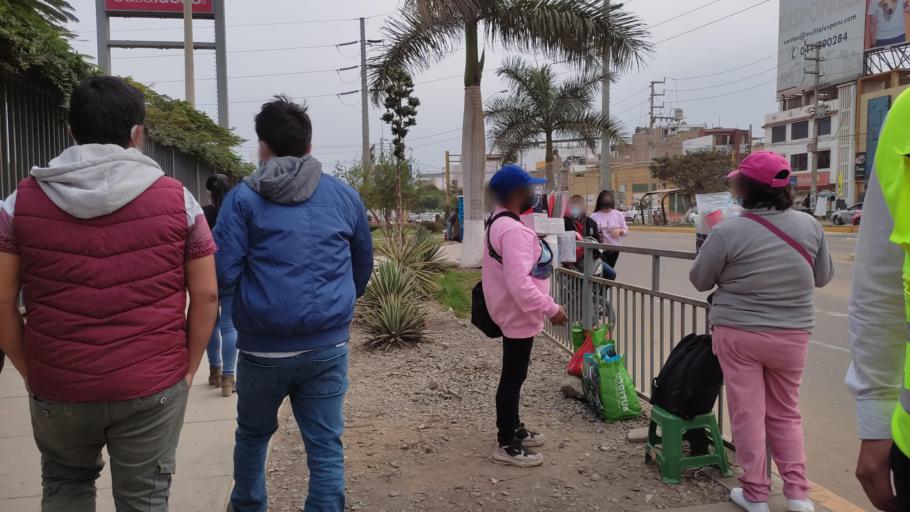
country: PE
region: La Libertad
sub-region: Provincia de Trujillo
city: Buenos Aires
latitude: -8.1316
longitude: -79.0324
